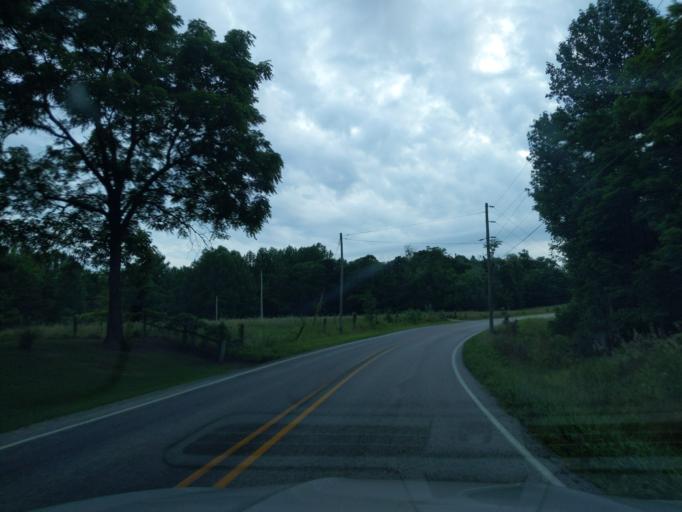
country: US
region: Indiana
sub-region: Ripley County
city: Osgood
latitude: 39.1947
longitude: -85.2603
